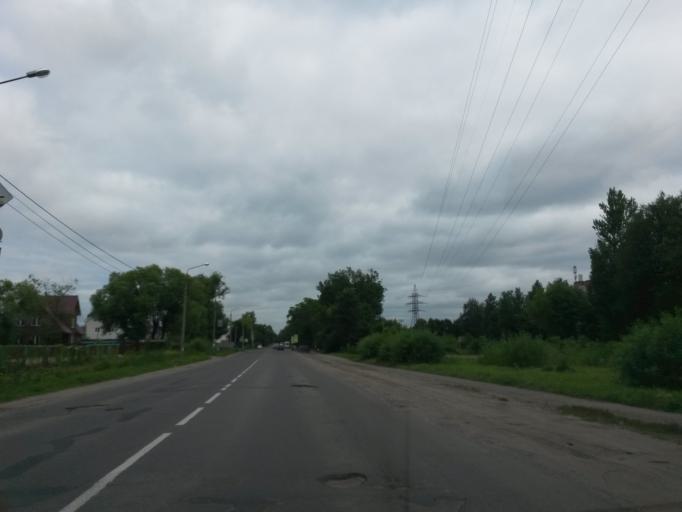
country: RU
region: Jaroslavl
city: Yaroslavl
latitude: 57.5875
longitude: 39.8764
